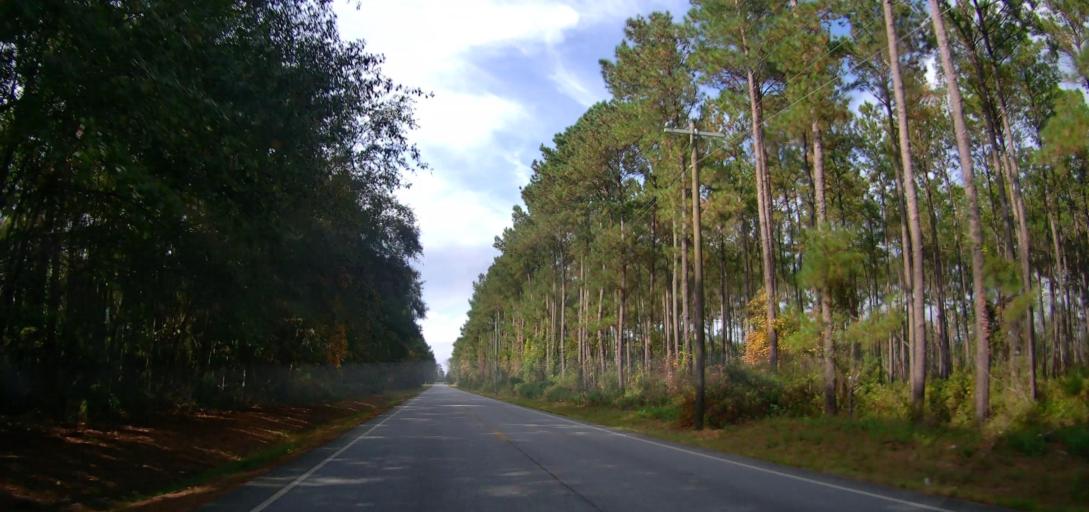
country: US
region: Georgia
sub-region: Thomas County
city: Thomasville
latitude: 30.9263
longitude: -84.0179
